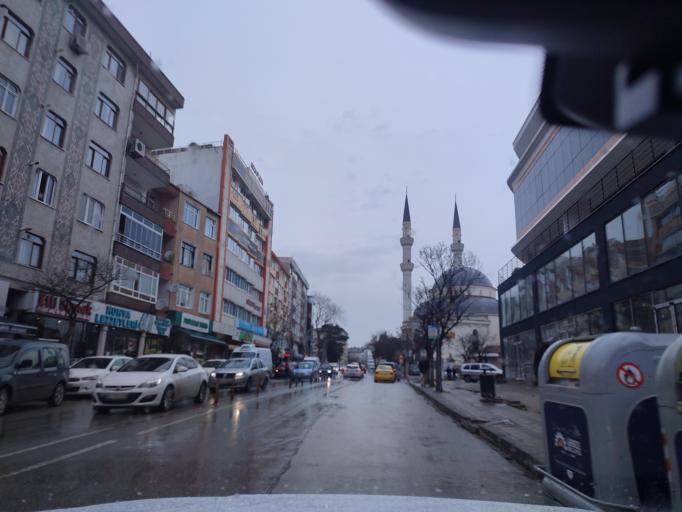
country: TR
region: Kocaeli
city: Gebze
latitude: 40.7985
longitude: 29.4403
